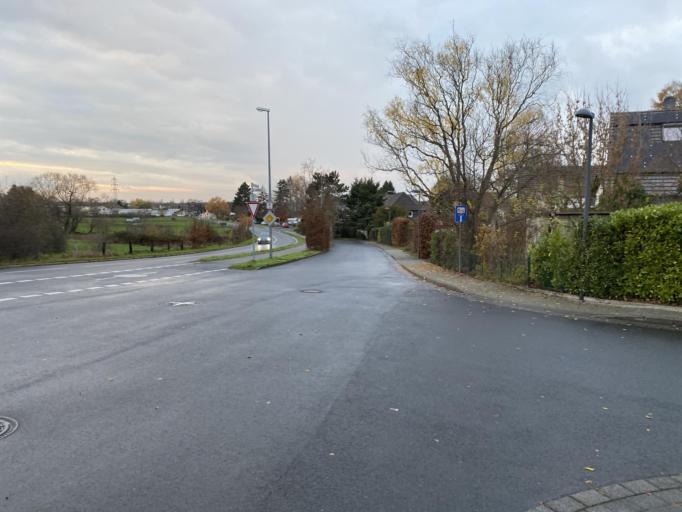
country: DE
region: North Rhine-Westphalia
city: Sankt Augustin
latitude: 50.7556
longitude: 7.1774
